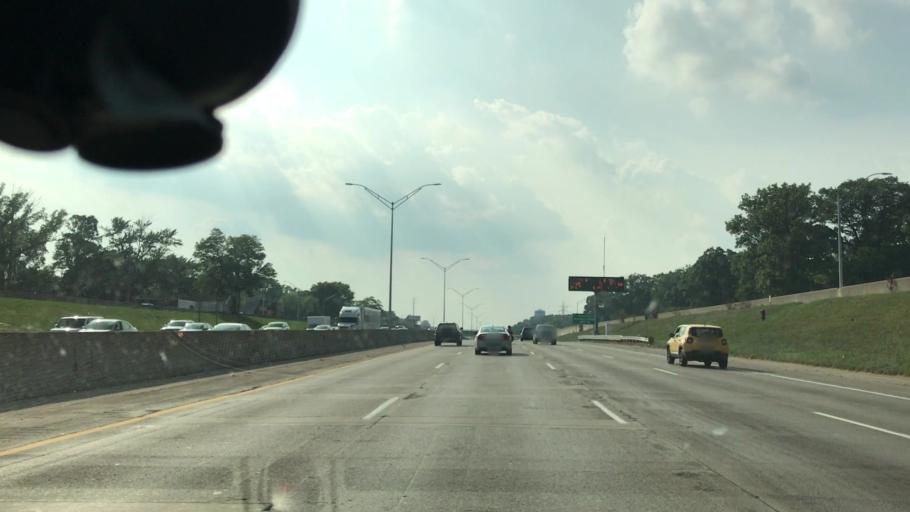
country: US
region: Michigan
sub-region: Oakland County
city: Pleasant Ridge
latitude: 42.4764
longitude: -83.1262
